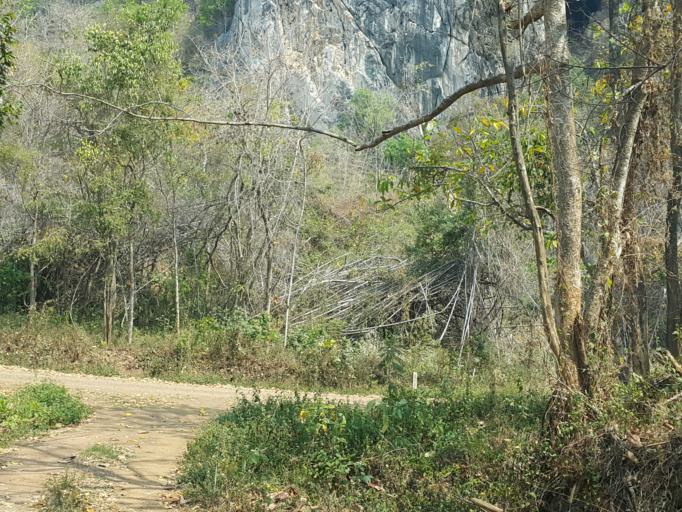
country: TH
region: Chiang Mai
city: Mae On
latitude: 18.7816
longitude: 99.2373
